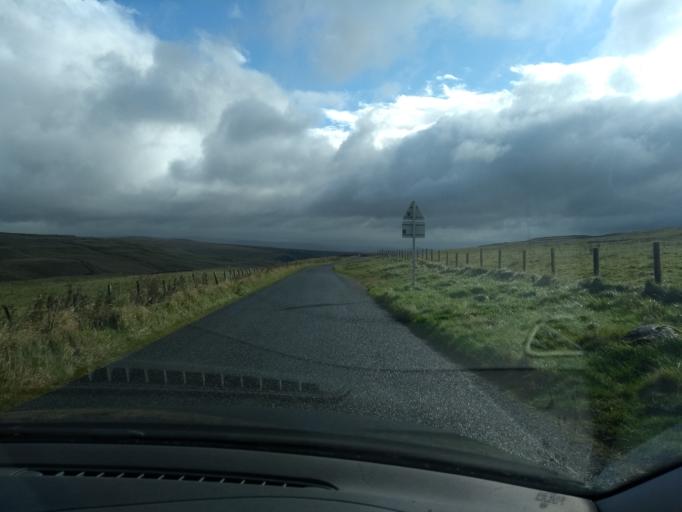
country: GB
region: England
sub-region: North Yorkshire
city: Settle
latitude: 54.0797
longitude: -2.1724
